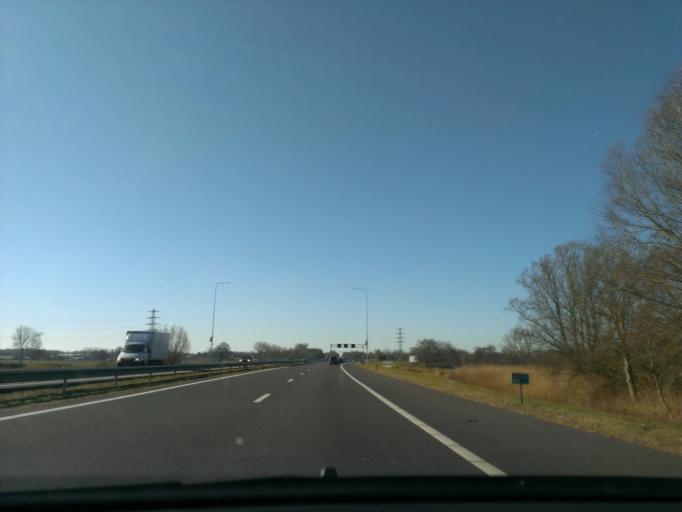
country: NL
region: Drenthe
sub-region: Gemeente Meppel
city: Meppel
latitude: 52.6857
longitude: 6.2028
